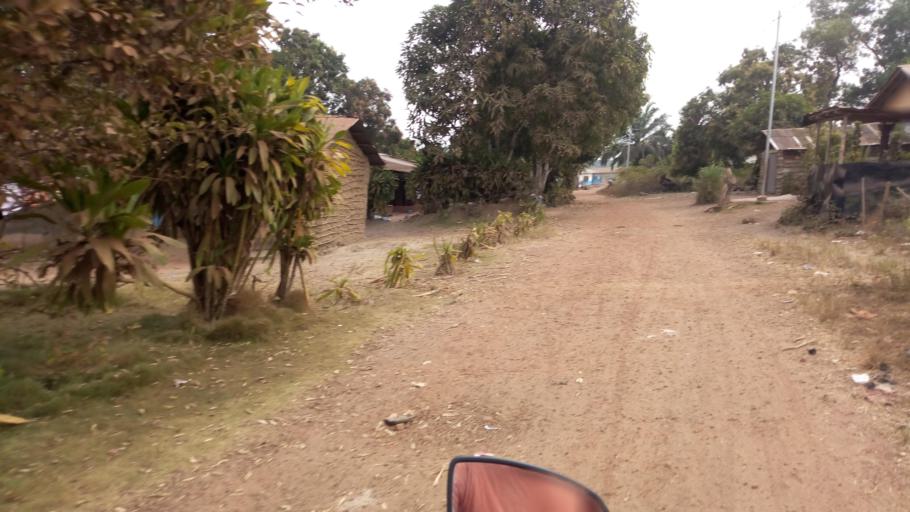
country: SL
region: Southern Province
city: Mogbwemo
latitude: 7.7889
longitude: -12.3038
